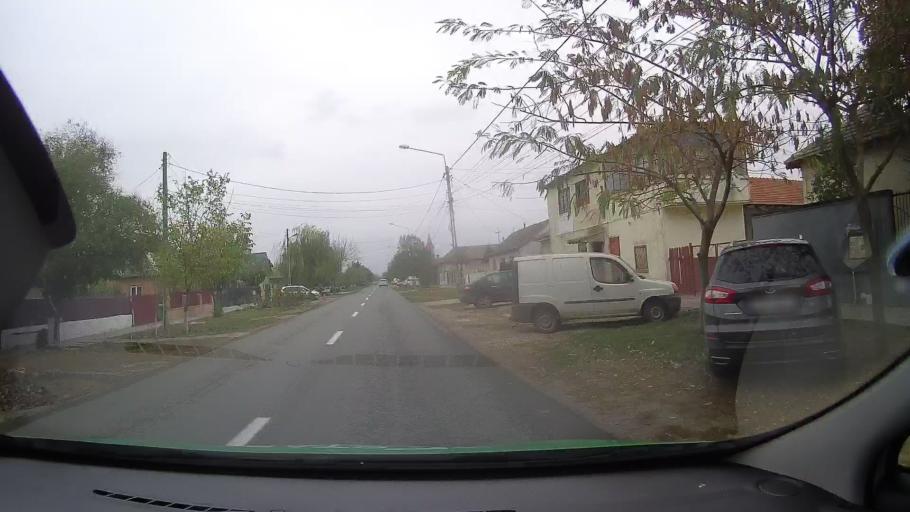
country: RO
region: Constanta
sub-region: Comuna Mihail Kogalniceanu
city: Mihail Kogalniceanu
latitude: 44.3705
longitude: 28.4634
